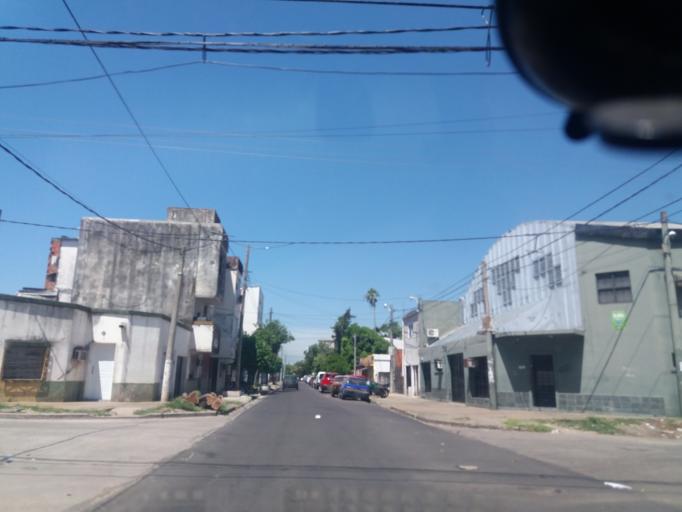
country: AR
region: Corrientes
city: Corrientes
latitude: -27.4795
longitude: -58.8450
